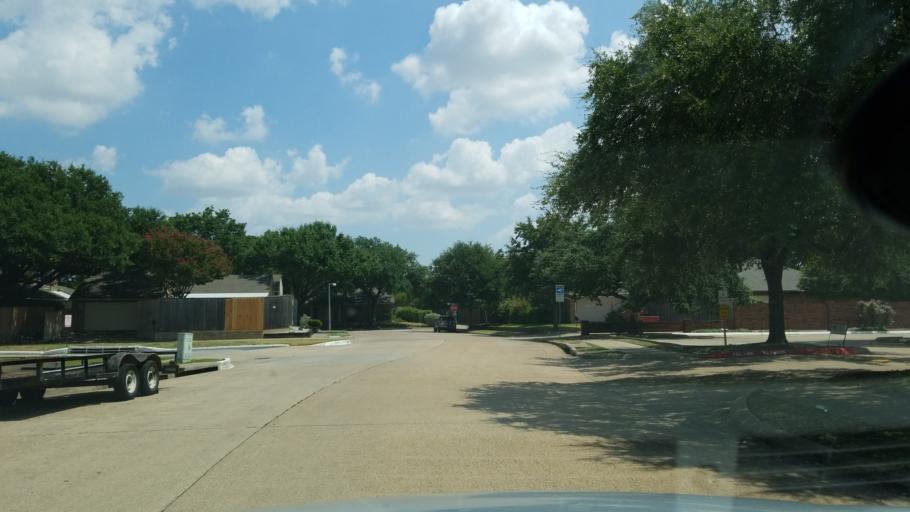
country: US
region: Texas
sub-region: Dallas County
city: Richardson
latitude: 32.9271
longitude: -96.7332
